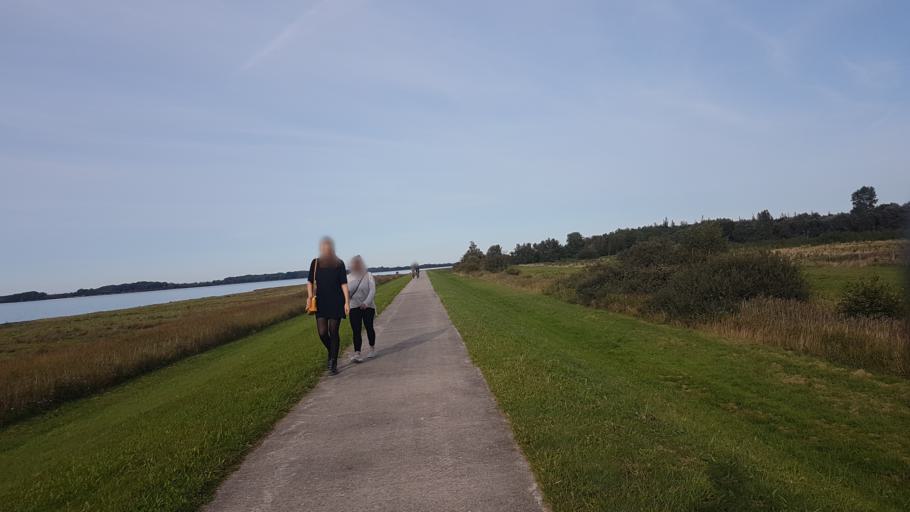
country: DE
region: Mecklenburg-Vorpommern
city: Hiddensee
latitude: 54.4852
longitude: 13.1563
